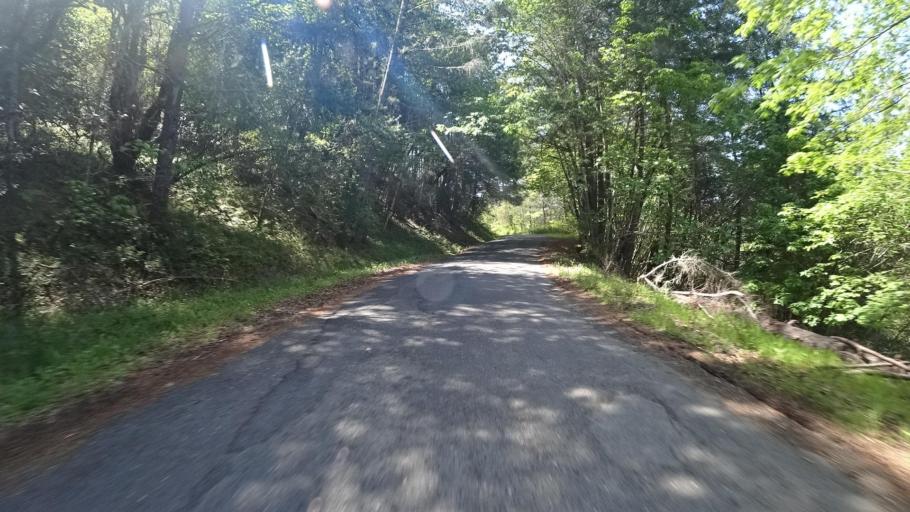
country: US
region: California
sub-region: Humboldt County
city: Redway
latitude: 40.1890
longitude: -123.5739
